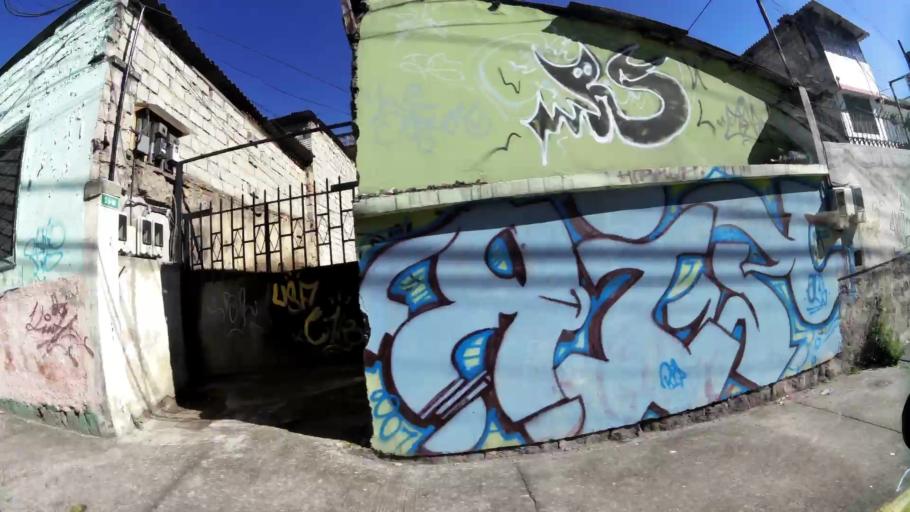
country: EC
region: Pichincha
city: Quito
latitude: -0.2348
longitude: -78.5243
